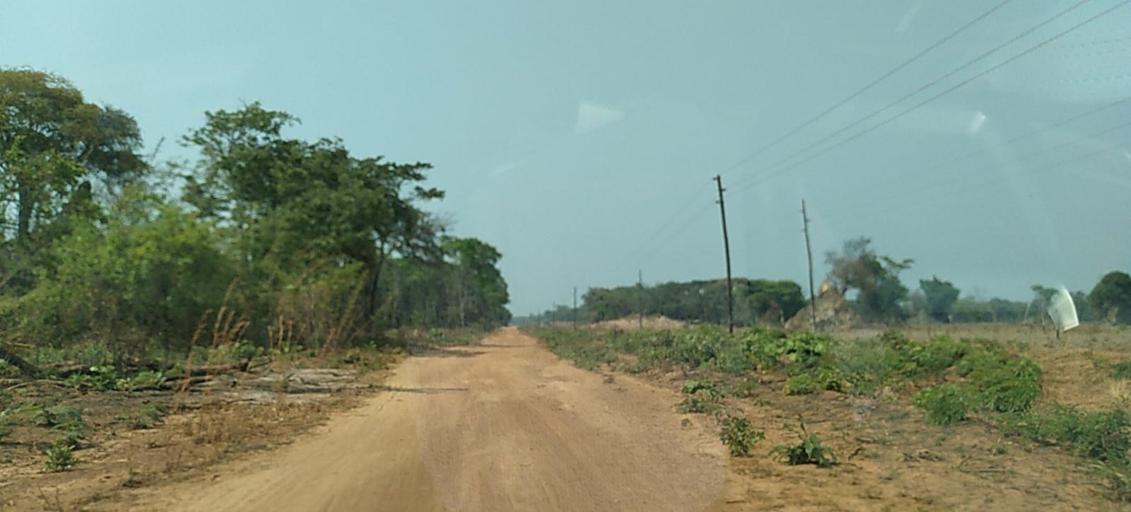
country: ZM
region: Copperbelt
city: Kalulushi
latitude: -13.0917
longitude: 27.4073
